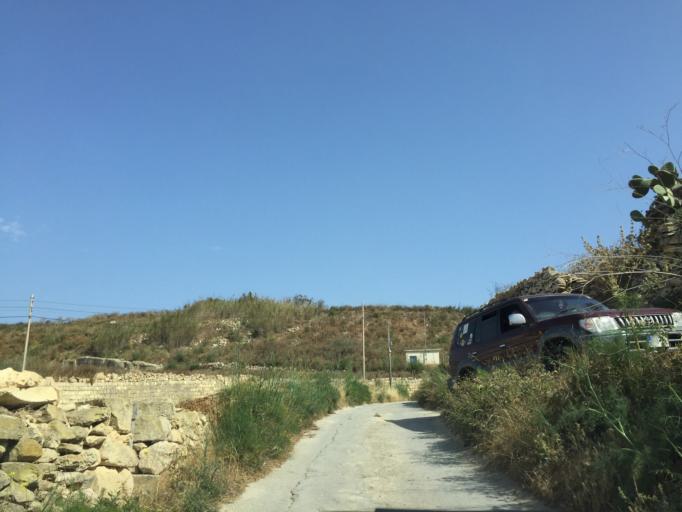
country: MT
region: L-Gharb
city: Gharb
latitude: 36.0671
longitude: 14.2057
